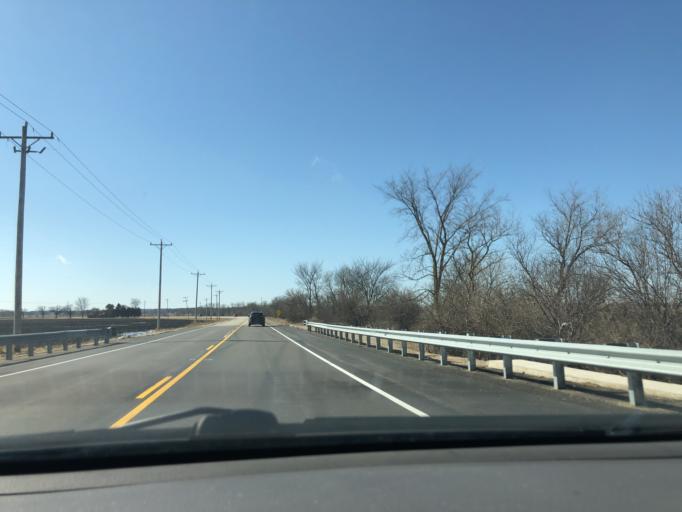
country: US
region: Illinois
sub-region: Kane County
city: Pingree Grove
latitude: 42.1076
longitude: -88.4504
